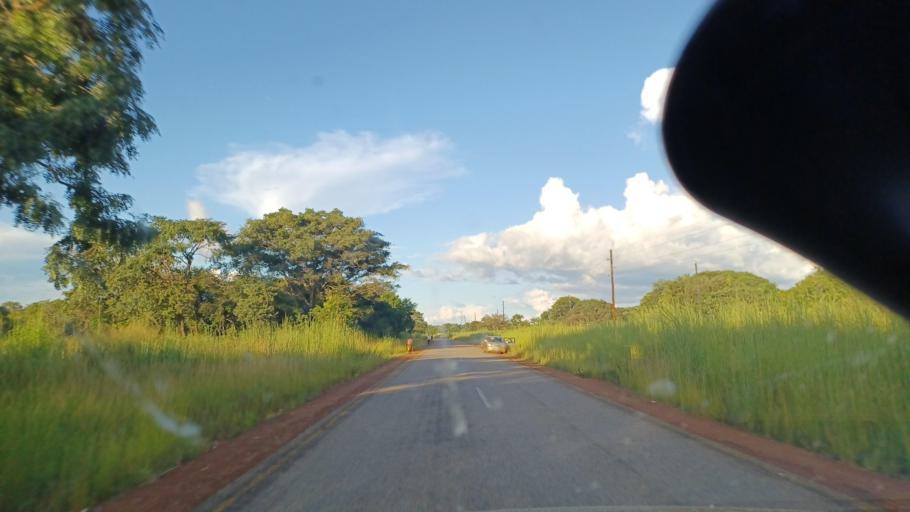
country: ZM
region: North-Western
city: Kalengwa
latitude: -13.1343
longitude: 25.1652
